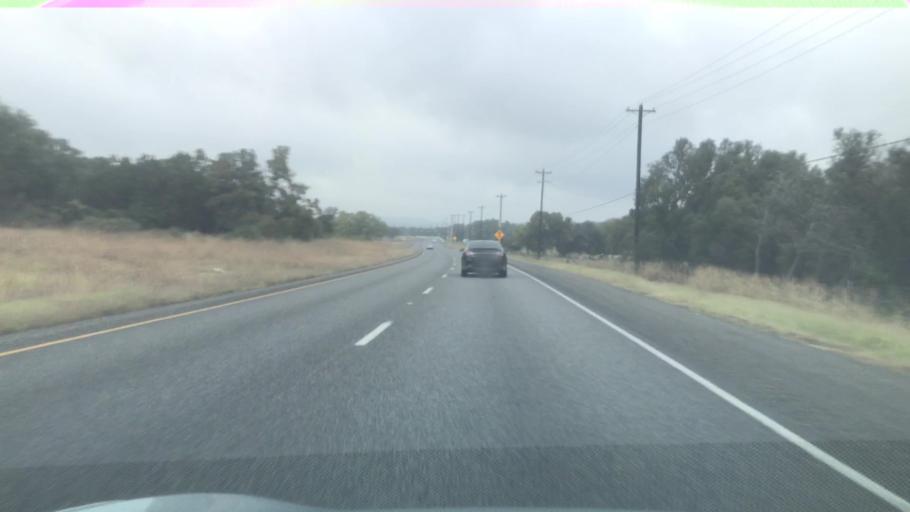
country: US
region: Texas
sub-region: Comal County
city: Bulverde
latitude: 29.8800
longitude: -98.4099
